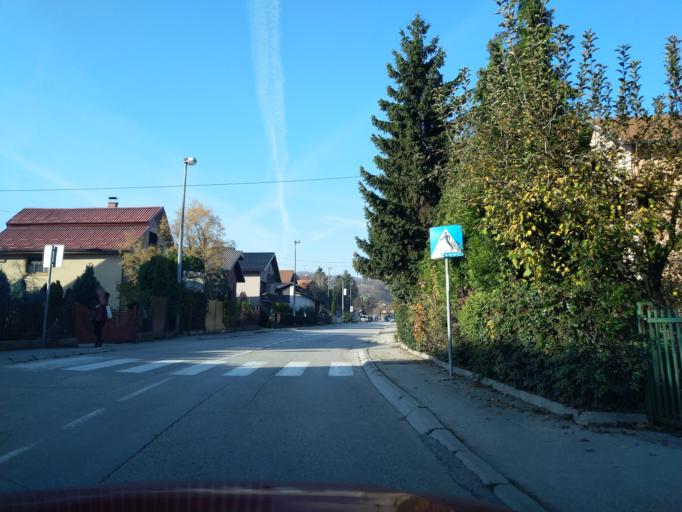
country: RS
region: Central Serbia
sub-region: Zlatiborski Okrug
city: Uzice
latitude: 43.8435
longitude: 19.8983
